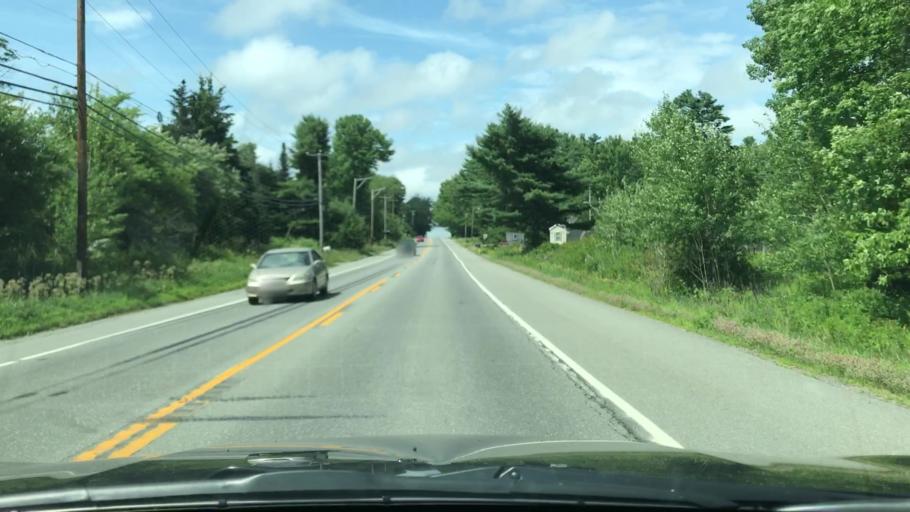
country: US
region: Maine
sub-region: Waldo County
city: Belfast
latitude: 44.3853
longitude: -68.9875
